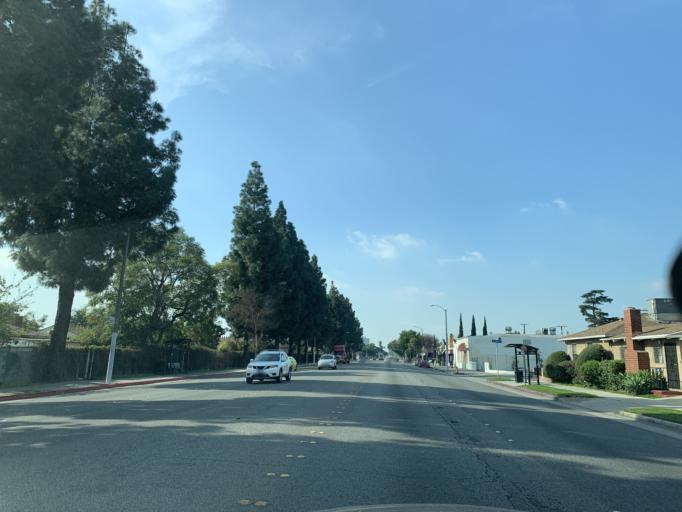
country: US
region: California
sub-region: Los Angeles County
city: Lynwood
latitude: 33.9317
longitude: -118.1942
